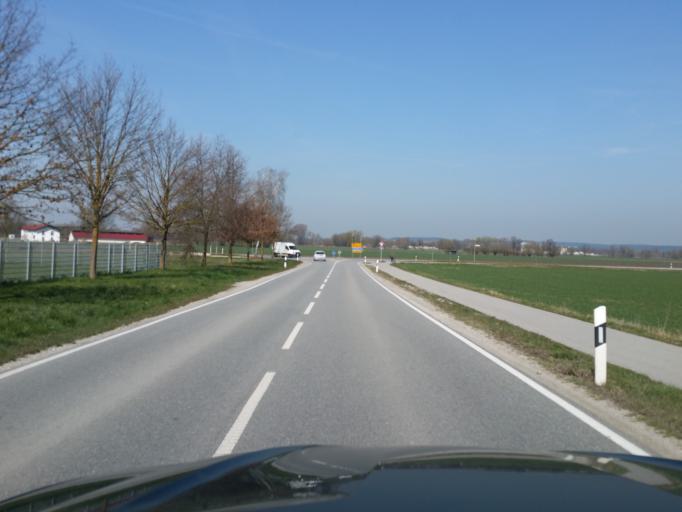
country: DE
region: Bavaria
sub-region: Upper Bavaria
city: Langenpreising
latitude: 48.4611
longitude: 12.0076
